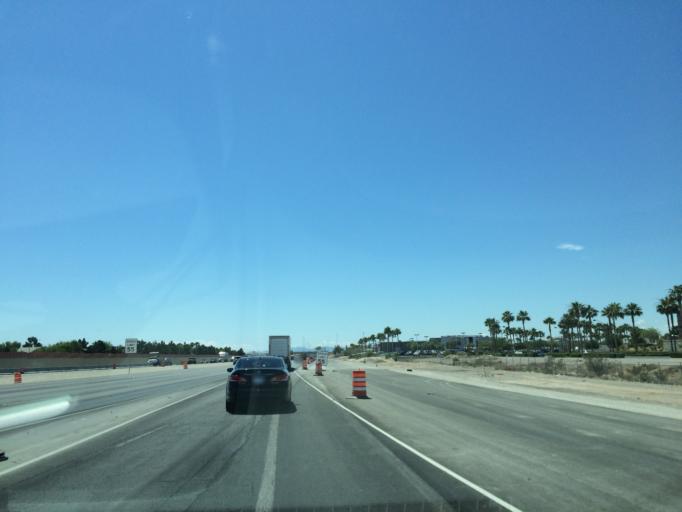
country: US
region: Nevada
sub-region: Clark County
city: Las Vegas
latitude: 36.2714
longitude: -115.2616
